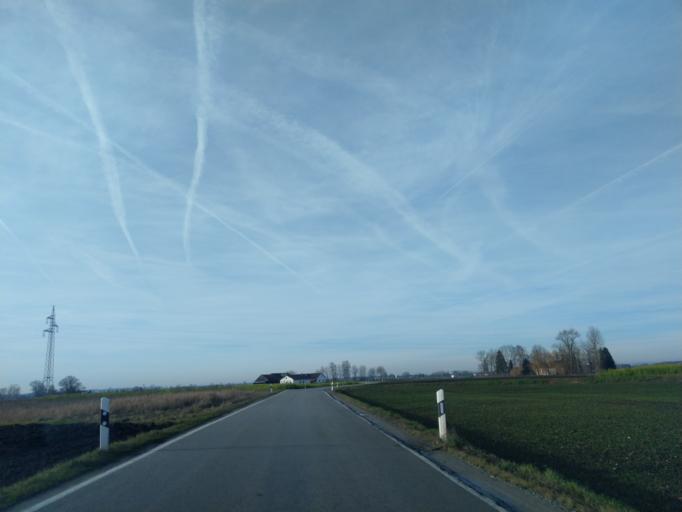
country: DE
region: Bavaria
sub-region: Lower Bavaria
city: Oberporing
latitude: 48.7155
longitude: 12.8017
